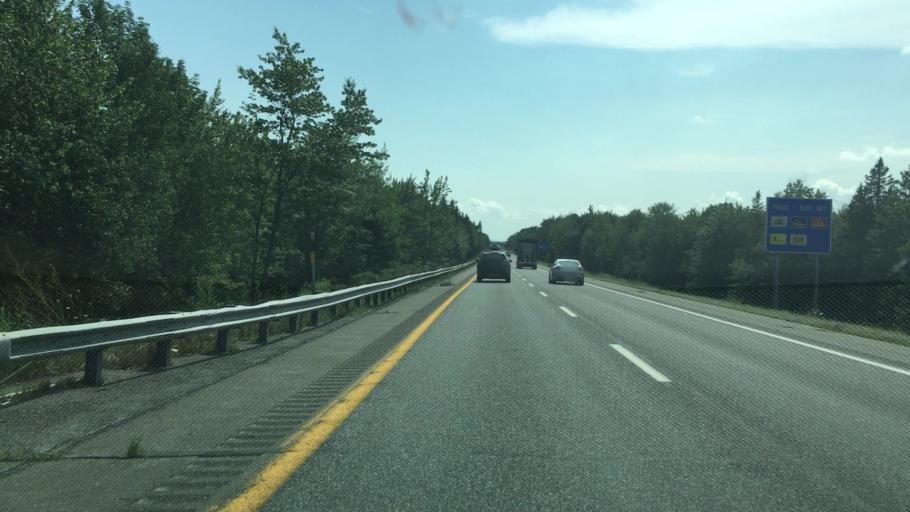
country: US
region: Maine
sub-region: Penobscot County
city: Veazie
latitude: 44.8550
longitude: -68.7236
